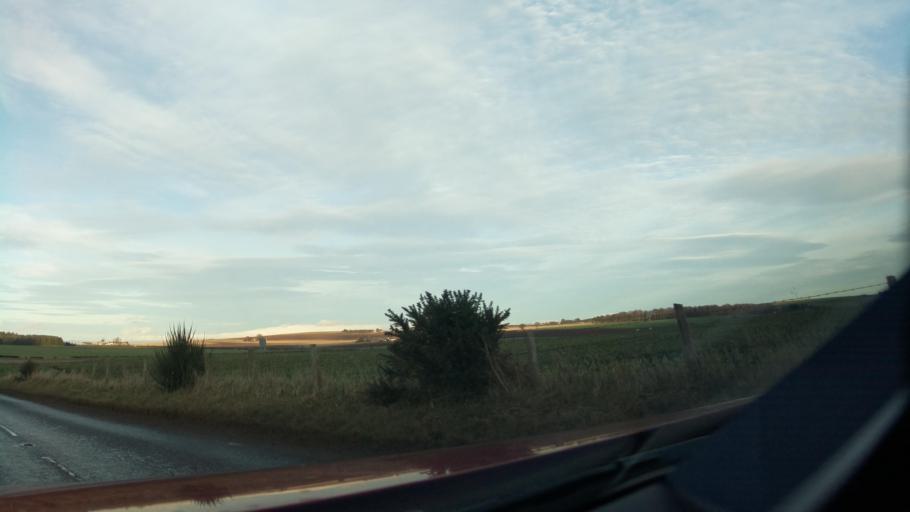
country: GB
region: Scotland
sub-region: Angus
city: Letham
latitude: 56.5755
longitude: -2.7801
